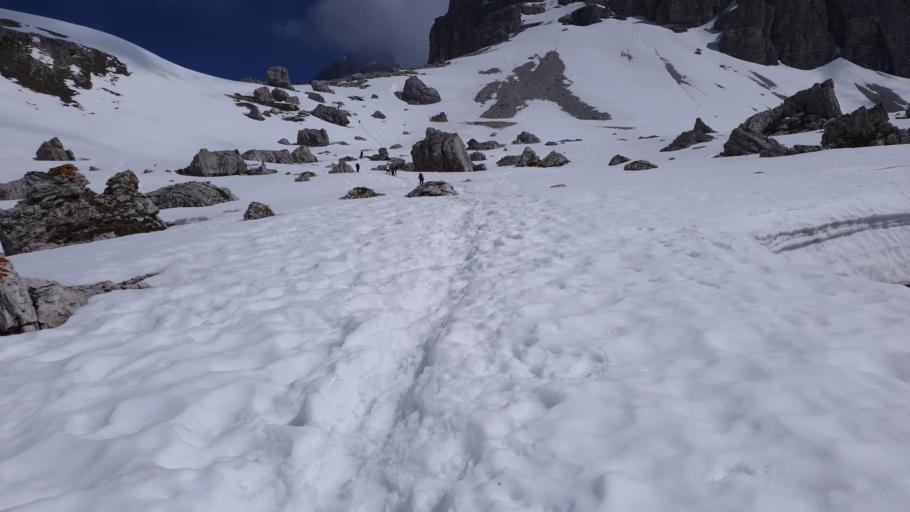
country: IT
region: Trentino-Alto Adige
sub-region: Bolzano
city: Sesto
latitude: 46.6200
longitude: 12.3126
